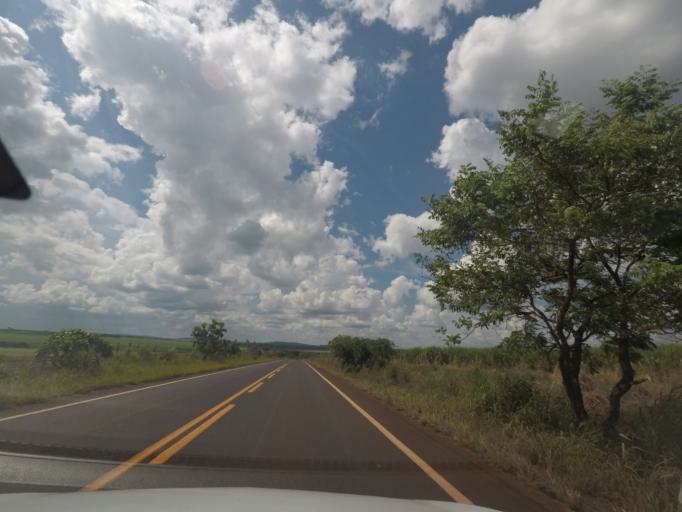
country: BR
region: Minas Gerais
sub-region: Conceicao Das Alagoas
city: Conceicao das Alagoas
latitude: -19.8261
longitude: -48.5918
